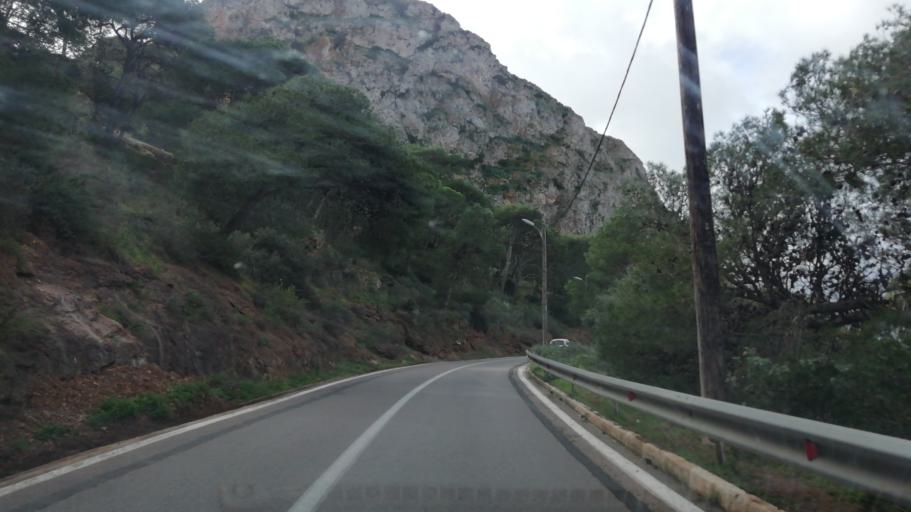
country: DZ
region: Oran
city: Oran
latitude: 35.7095
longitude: -0.6679
